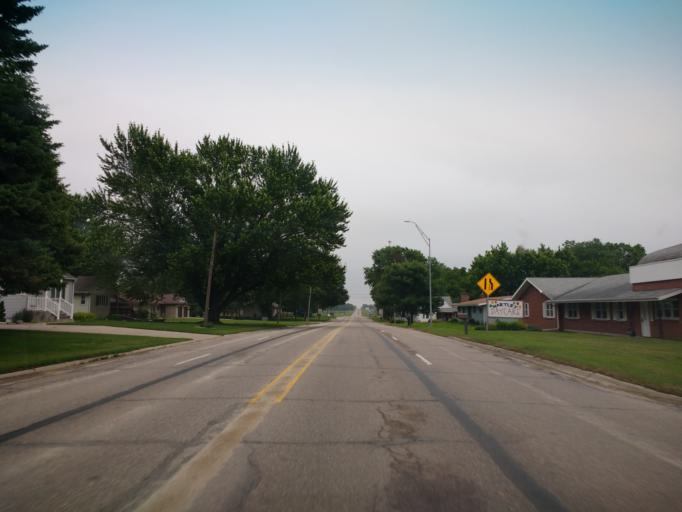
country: US
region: Iowa
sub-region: O'Brien County
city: Hartley
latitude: 43.1848
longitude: -95.4700
